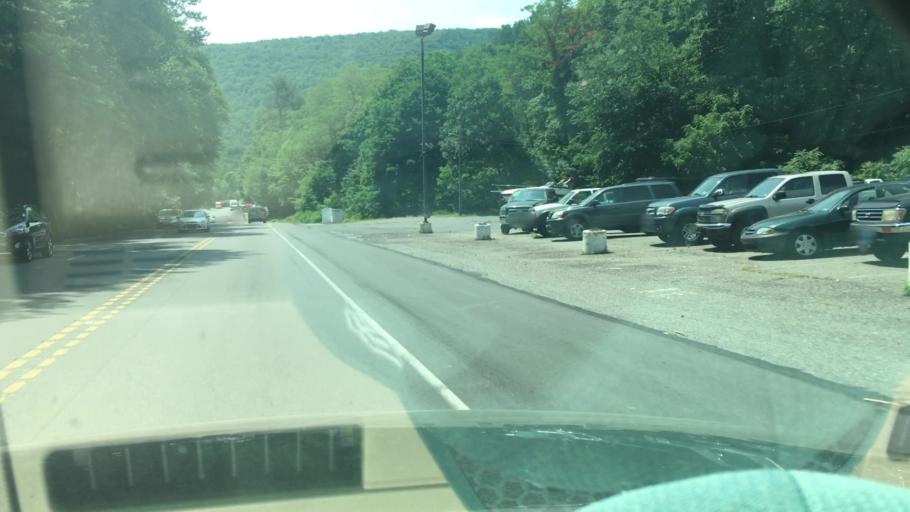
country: US
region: Pennsylvania
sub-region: Schuylkill County
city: Hometown
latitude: 40.8188
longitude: -75.9787
